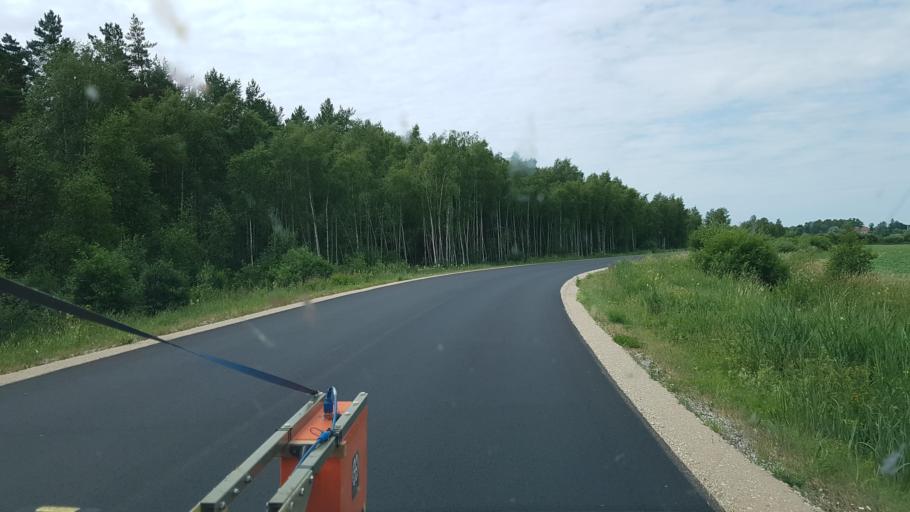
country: EE
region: Paernumaa
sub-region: Audru vald
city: Audru
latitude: 58.6163
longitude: 24.2273
